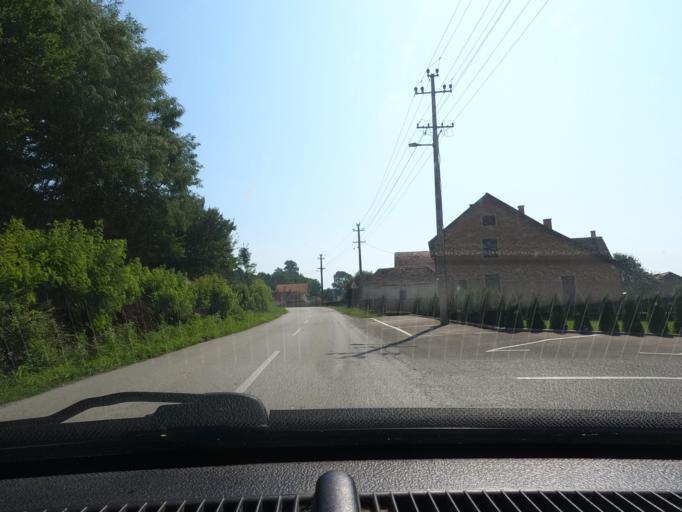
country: RS
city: Jadranska Lesnica
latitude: 44.5482
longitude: 19.3457
